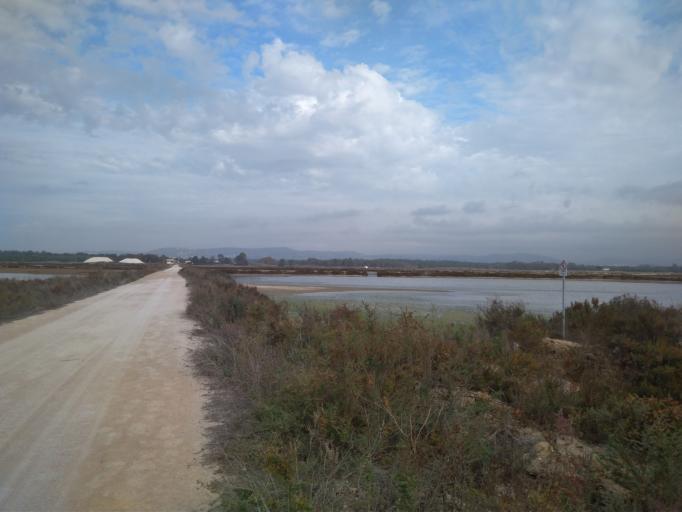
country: PT
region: Faro
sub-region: Faro
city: Faro
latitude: 37.0216
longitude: -7.9970
